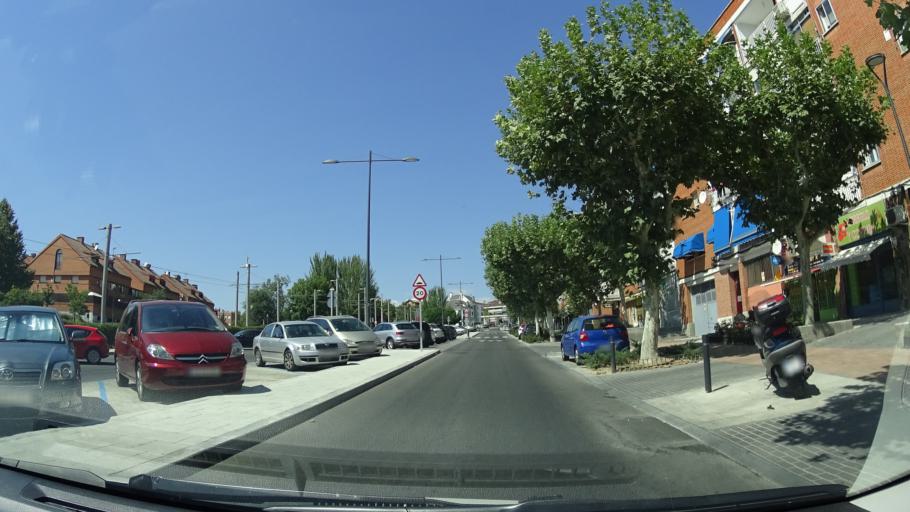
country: ES
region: Madrid
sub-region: Provincia de Madrid
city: Boadilla del Monte
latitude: 40.4064
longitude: -3.8788
